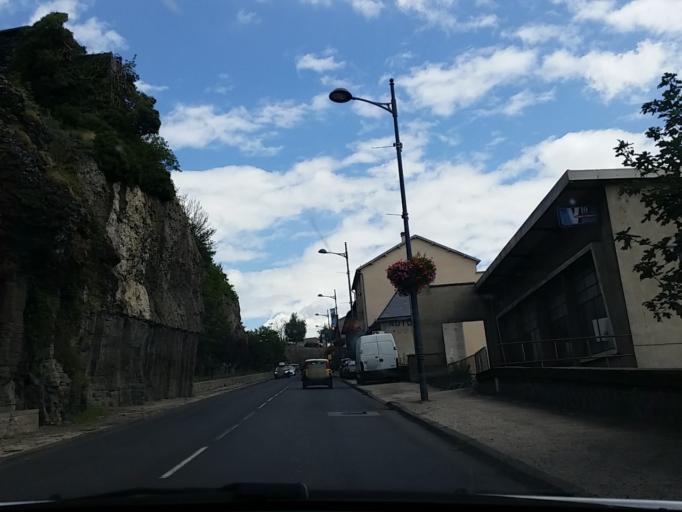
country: FR
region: Auvergne
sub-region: Departement du Cantal
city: Saint-Flour
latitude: 45.0323
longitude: 3.0848
